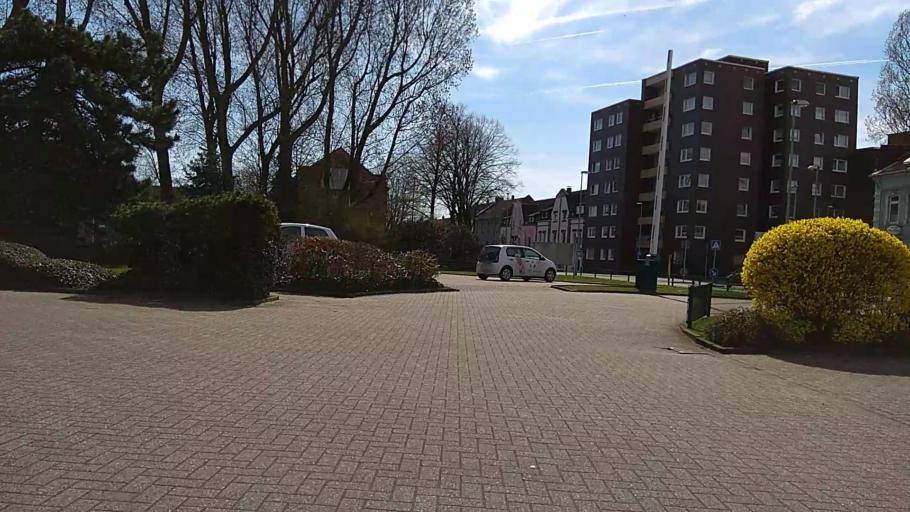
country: DE
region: North Rhine-Westphalia
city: Herten
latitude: 51.5639
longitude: 7.0895
